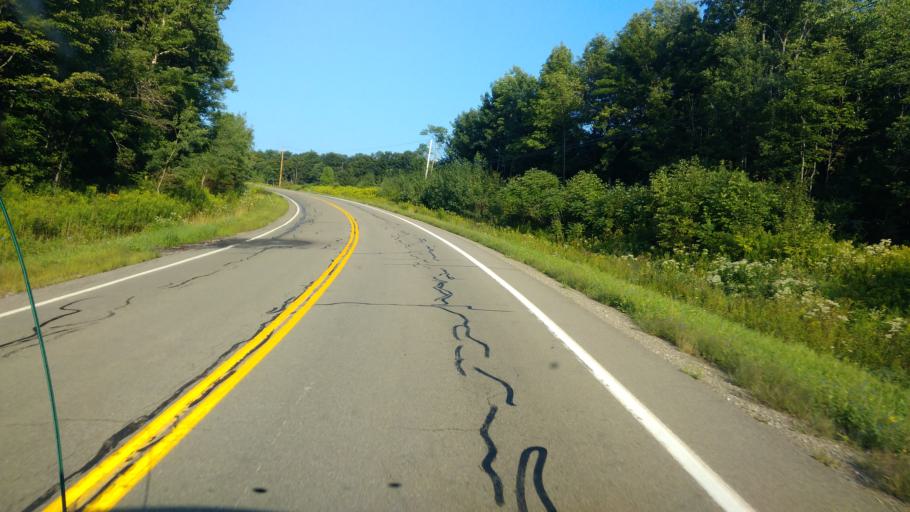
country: US
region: New York
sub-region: Allegany County
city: Andover
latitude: 42.1540
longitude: -77.6993
